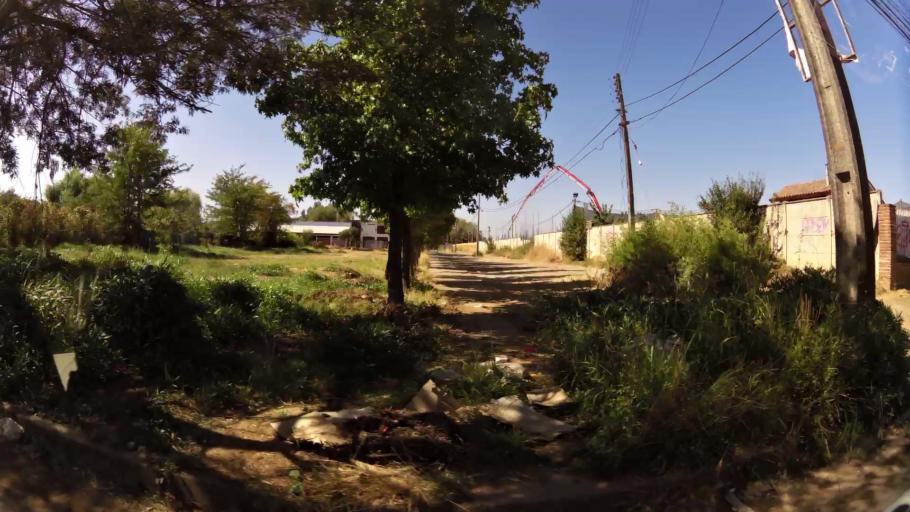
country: CL
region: Maule
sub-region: Provincia de Talca
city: Talca
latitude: -35.4285
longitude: -71.6231
